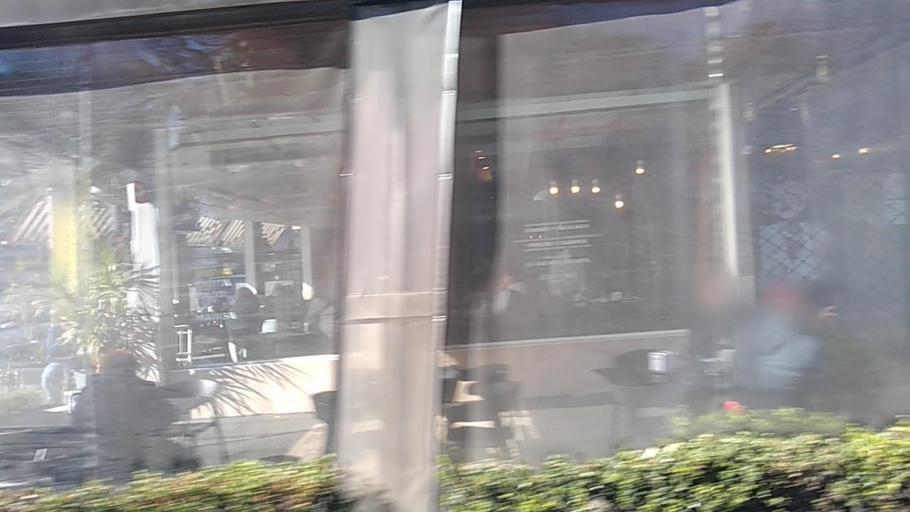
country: AR
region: Buenos Aires F.D.
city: Villa Santa Rita
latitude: -34.6193
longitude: -58.5049
